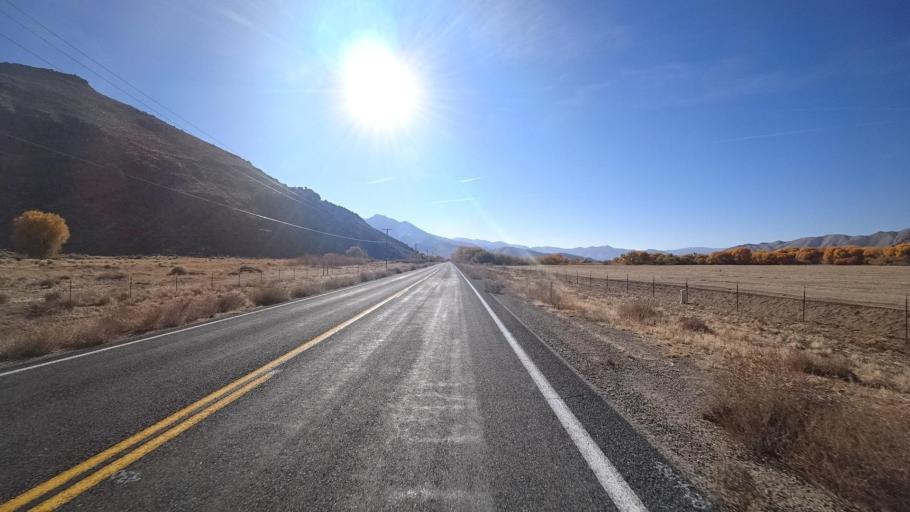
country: US
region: California
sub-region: Kern County
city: Weldon
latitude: 35.6832
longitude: -118.2472
